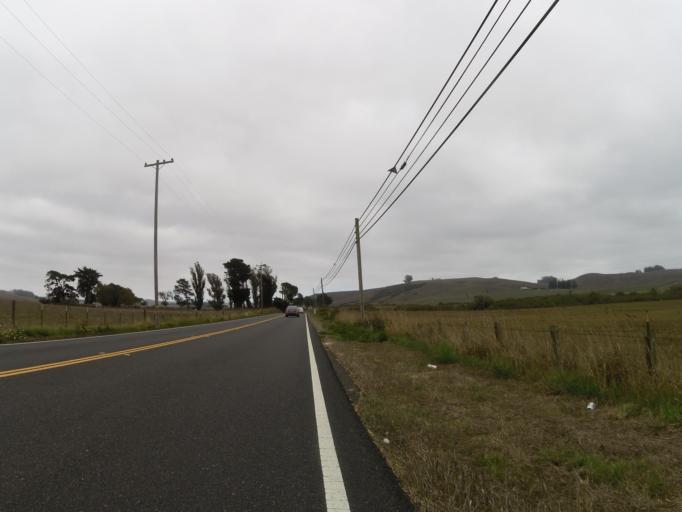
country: US
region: California
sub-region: Sonoma County
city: Occidental
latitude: 38.3186
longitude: -122.9010
